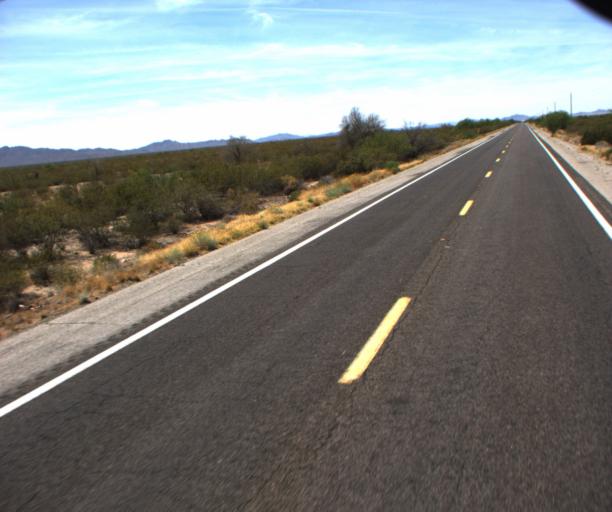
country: US
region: Arizona
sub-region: La Paz County
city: Salome
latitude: 33.8613
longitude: -113.4191
